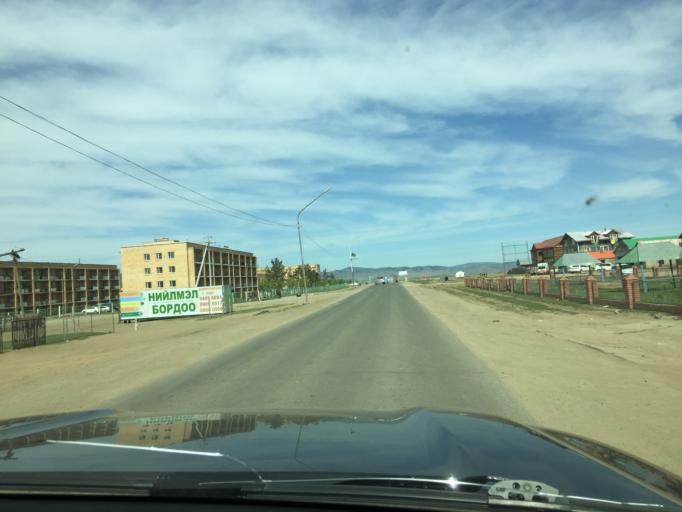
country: MN
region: Central Aimak
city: Ihsueuej
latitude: 48.2250
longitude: 106.2922
